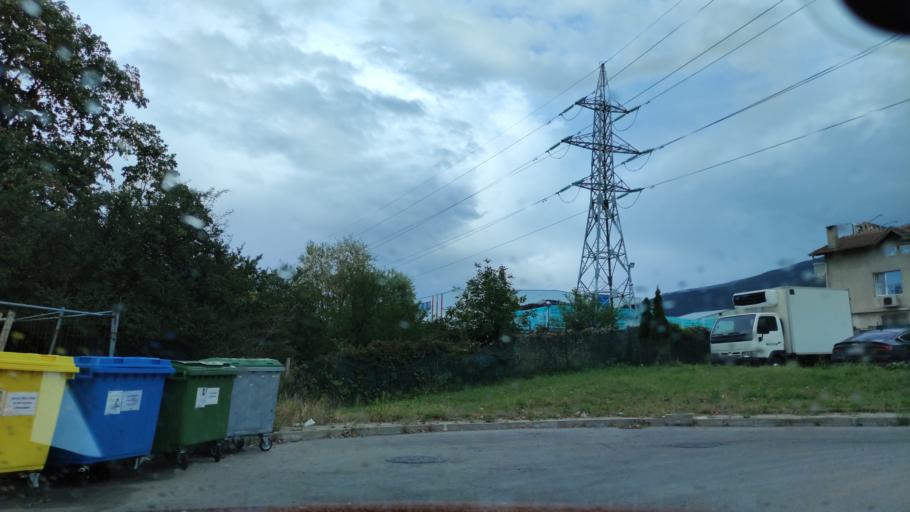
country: BG
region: Sofia-Capital
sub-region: Stolichna Obshtina
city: Sofia
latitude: 42.6528
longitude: 23.2881
